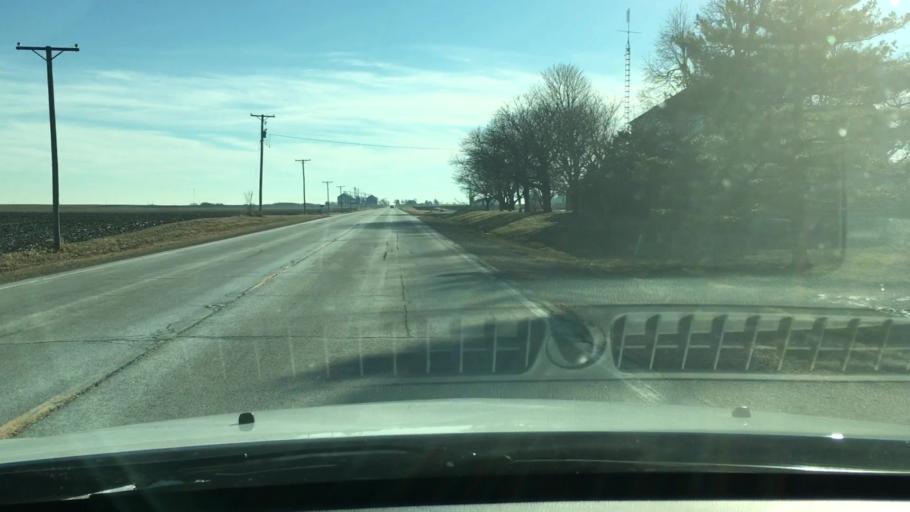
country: US
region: Illinois
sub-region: LaSalle County
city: Mendota
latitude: 41.6092
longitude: -89.1288
